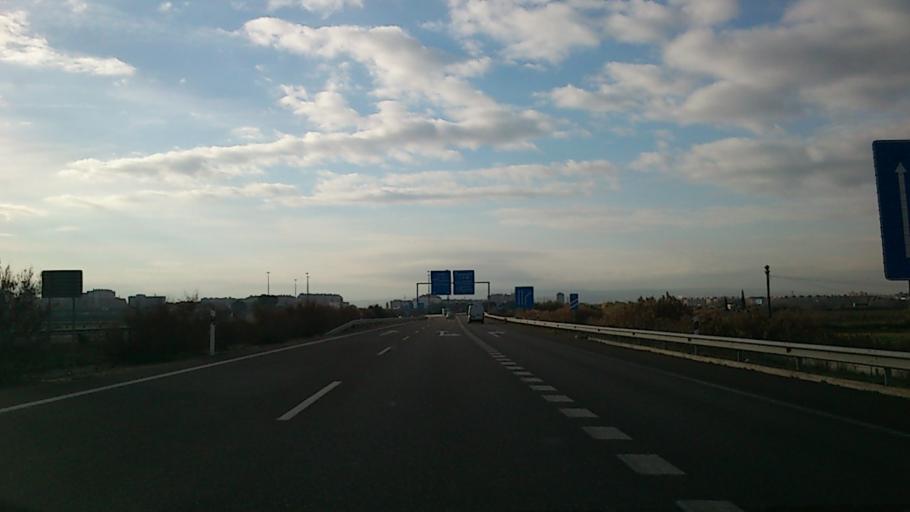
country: ES
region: Aragon
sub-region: Provincia de Zaragoza
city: Zaragoza
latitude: 41.6836
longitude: -0.8334
